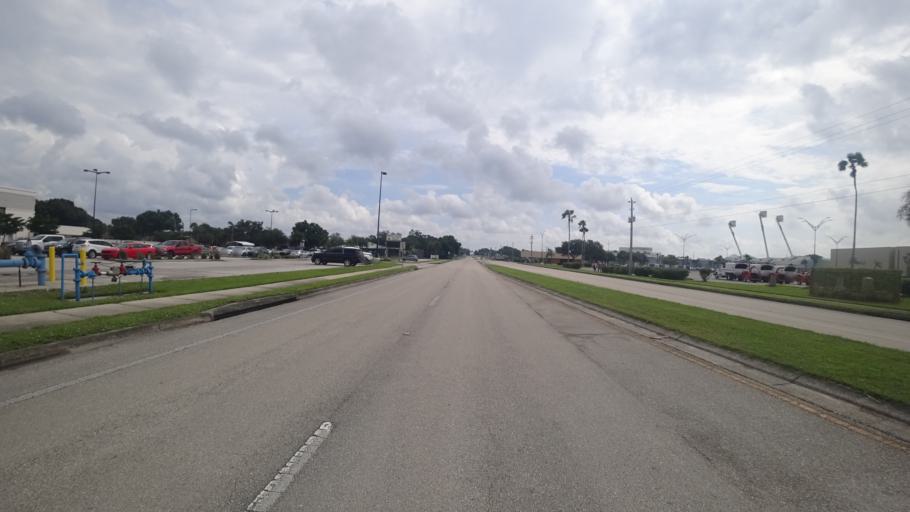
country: US
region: Florida
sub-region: Manatee County
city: West Samoset
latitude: 27.4690
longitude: -82.5677
